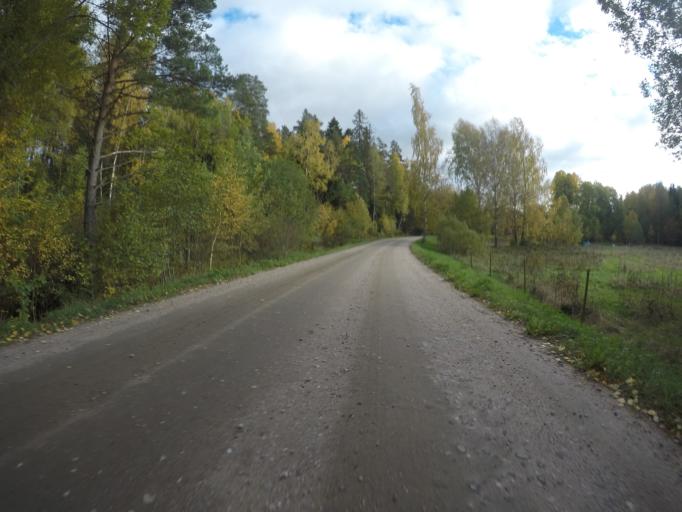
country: SE
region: Vaestmanland
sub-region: Arboga Kommun
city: Tyringe
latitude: 59.3805
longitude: 15.9476
